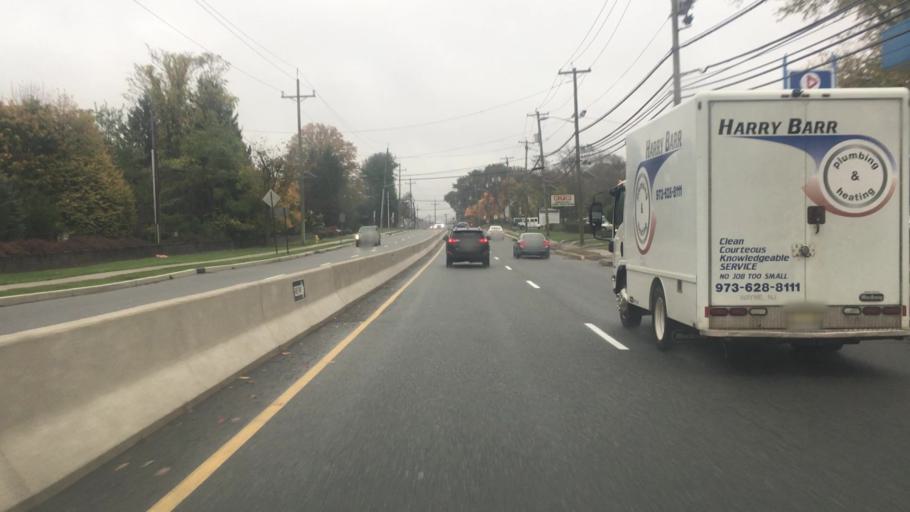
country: US
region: New Jersey
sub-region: Passaic County
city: Wayne
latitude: 40.9629
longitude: -74.2517
